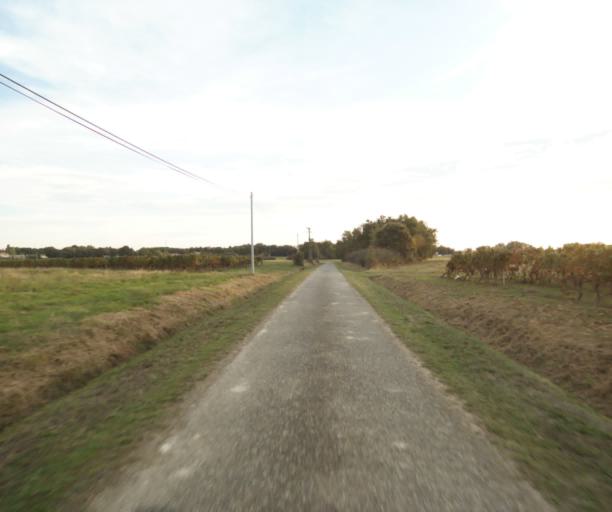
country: FR
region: Midi-Pyrenees
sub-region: Departement du Tarn-et-Garonne
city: Pompignan
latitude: 43.8222
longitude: 1.3232
